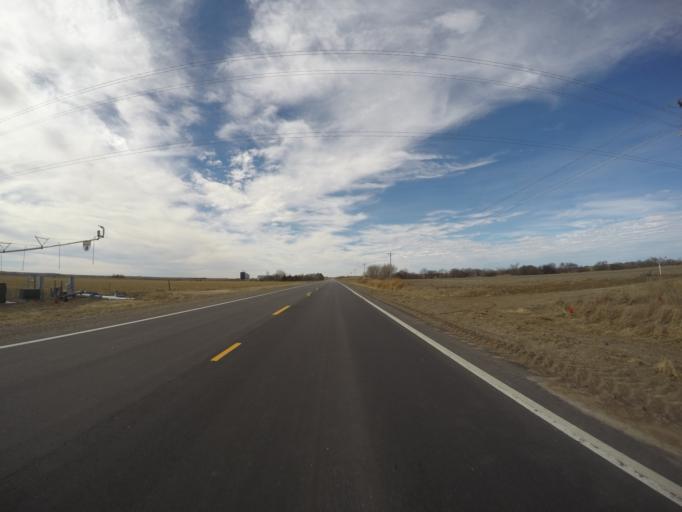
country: US
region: Nebraska
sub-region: Franklin County
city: Franklin
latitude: 40.0963
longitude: -98.8484
